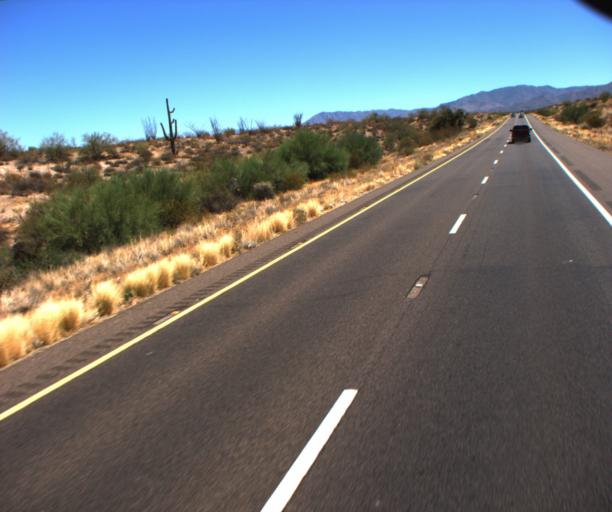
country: US
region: Arizona
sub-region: Maricopa County
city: Rio Verde
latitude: 33.6417
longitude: -111.5390
